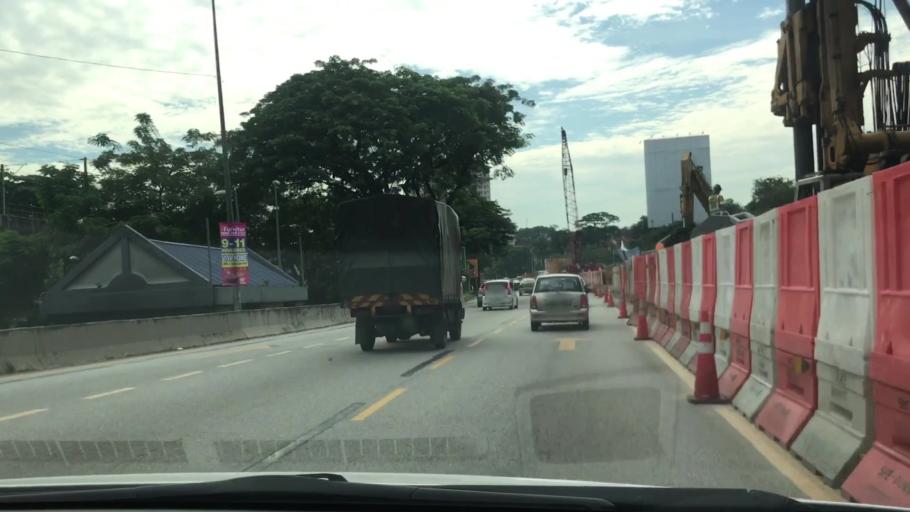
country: MY
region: Kuala Lumpur
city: Kuala Lumpur
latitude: 3.1140
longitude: 101.6803
